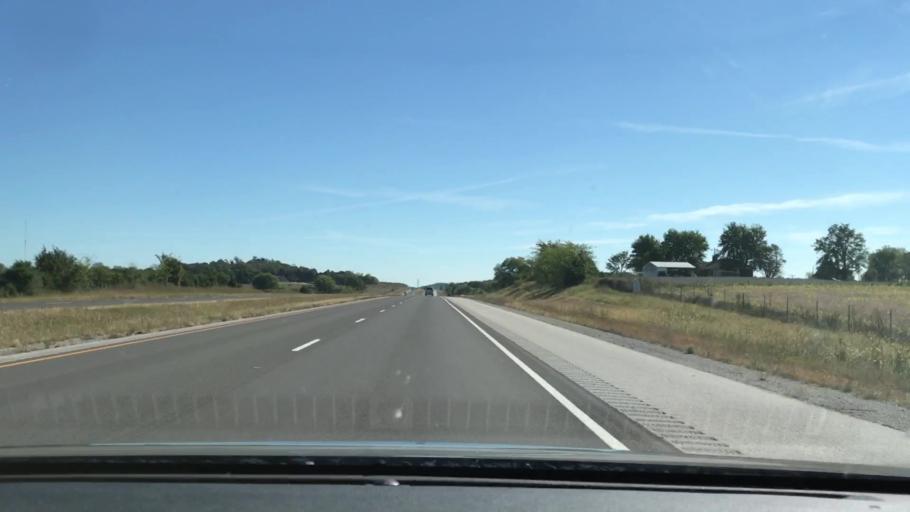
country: US
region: Kentucky
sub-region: Logan County
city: Russellville
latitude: 36.8365
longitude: -86.9495
